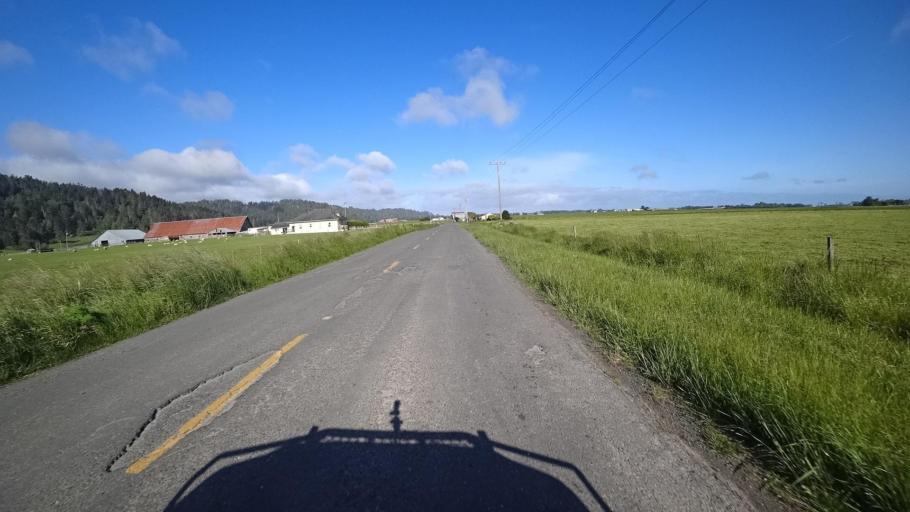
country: US
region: California
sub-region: Humboldt County
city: Ferndale
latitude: 40.5719
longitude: -124.2296
